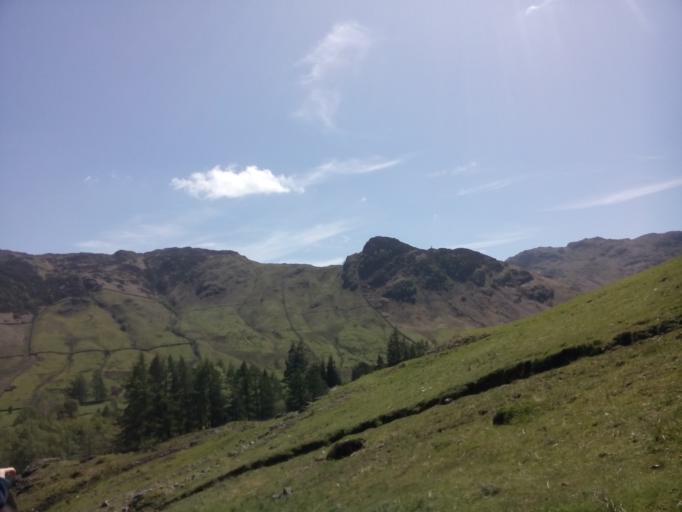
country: GB
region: England
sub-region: Cumbria
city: Ambleside
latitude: 54.4498
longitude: -3.0917
